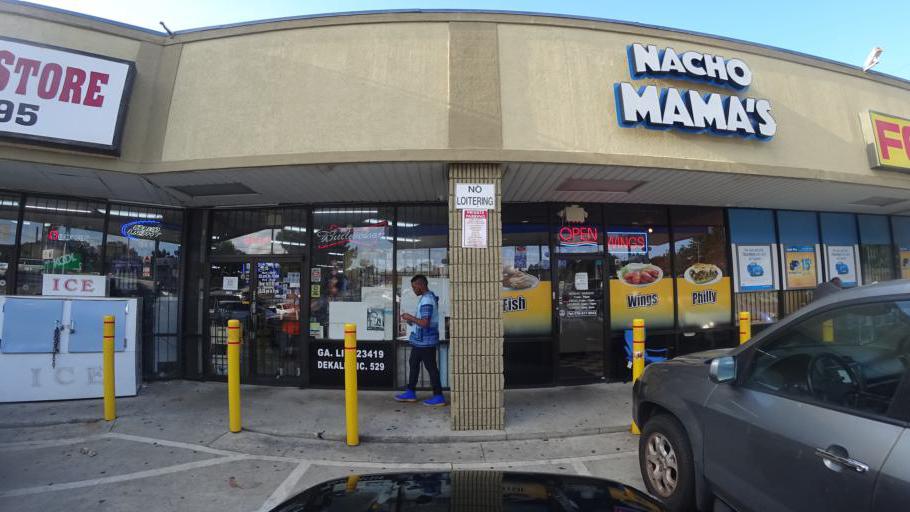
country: US
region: Georgia
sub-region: DeKalb County
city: Redan
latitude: 33.7571
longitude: -84.1659
